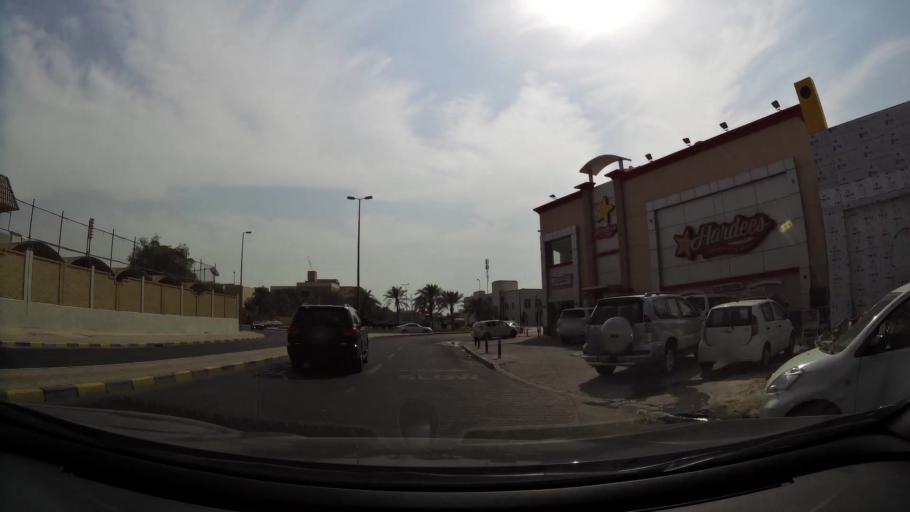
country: KW
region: Al Asimah
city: Ash Shamiyah
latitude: 29.3564
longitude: 47.9686
